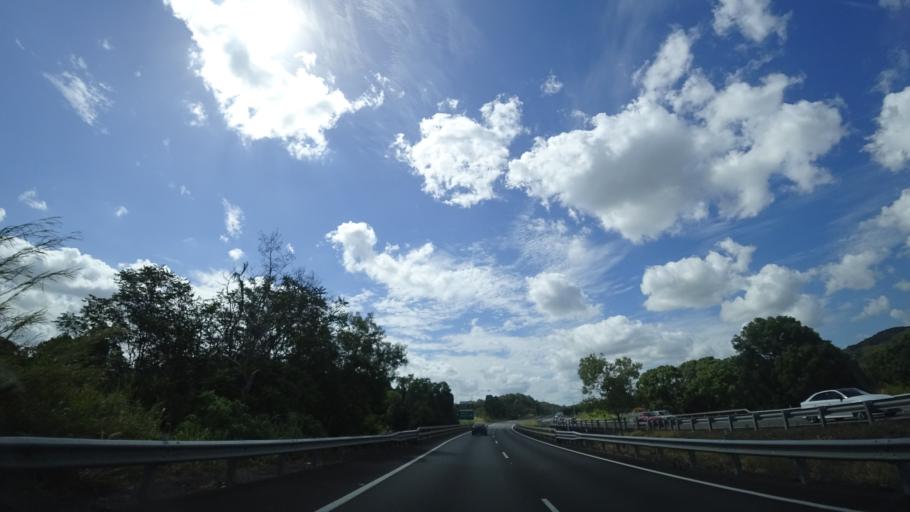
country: AU
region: Queensland
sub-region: Sunshine Coast
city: Twin Waters
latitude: -26.6190
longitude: 152.9824
